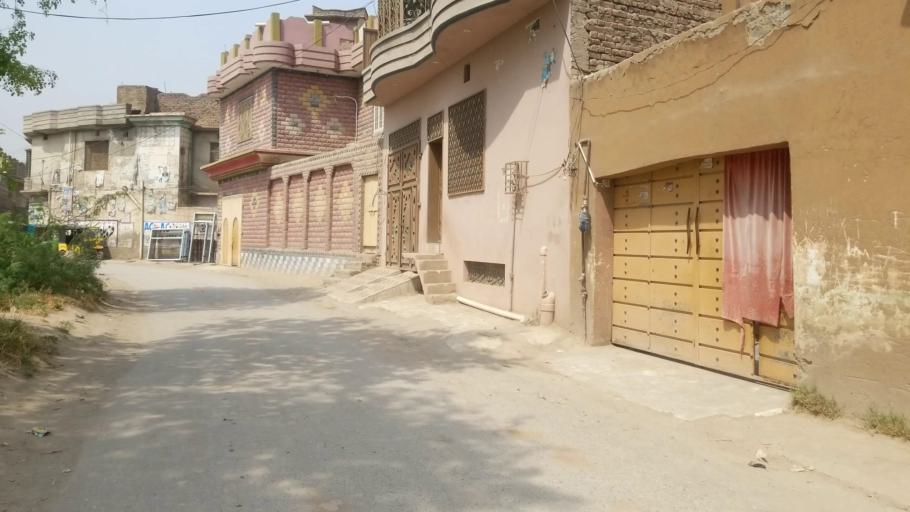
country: PK
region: Khyber Pakhtunkhwa
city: Peshawar
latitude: 33.9838
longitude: 71.5375
